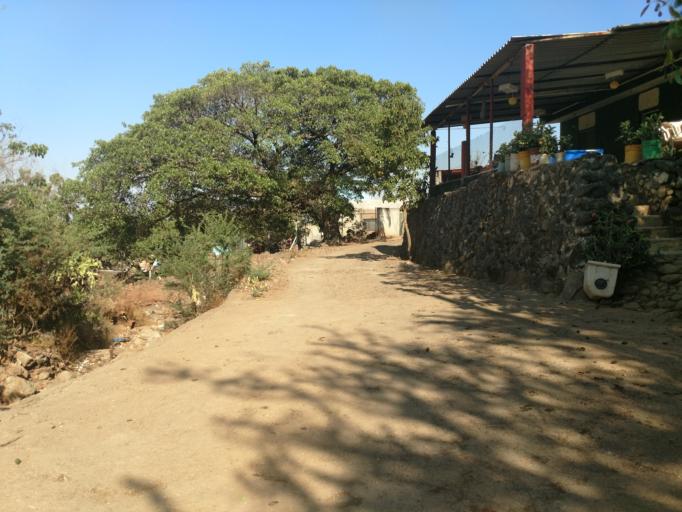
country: MX
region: Nayarit
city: Santa Maria del Oro
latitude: 21.4673
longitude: -104.6551
